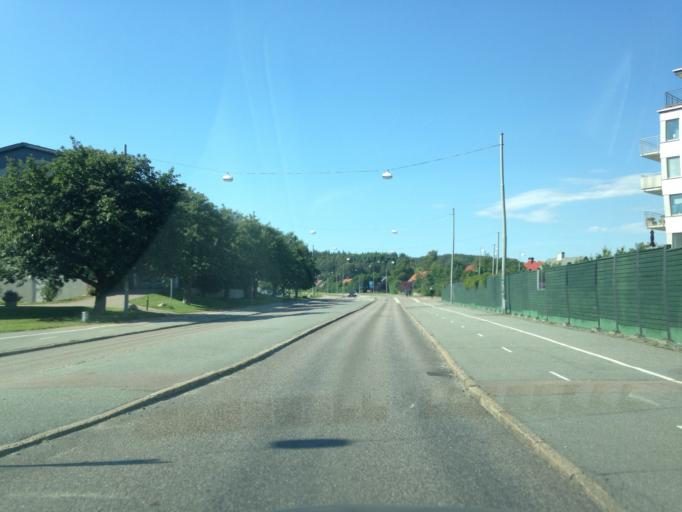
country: SE
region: Vaestra Goetaland
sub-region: Goteborg
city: Majorna
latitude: 57.7172
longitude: 11.9087
